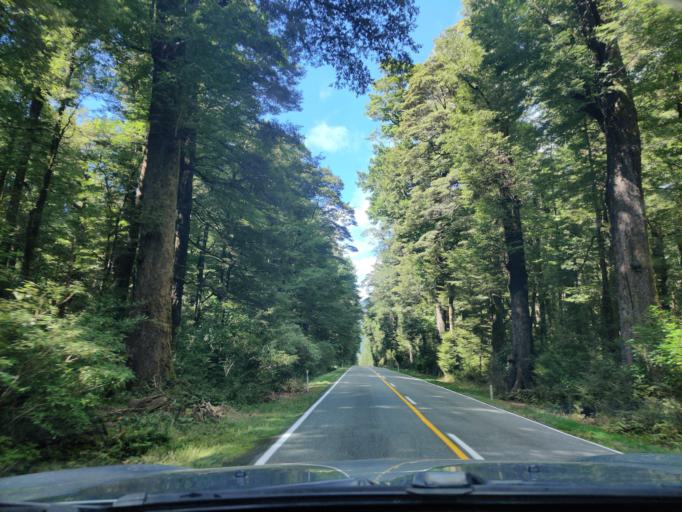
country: NZ
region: Canterbury
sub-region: Hurunui District
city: Amberley
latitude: -42.3807
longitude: 172.3067
